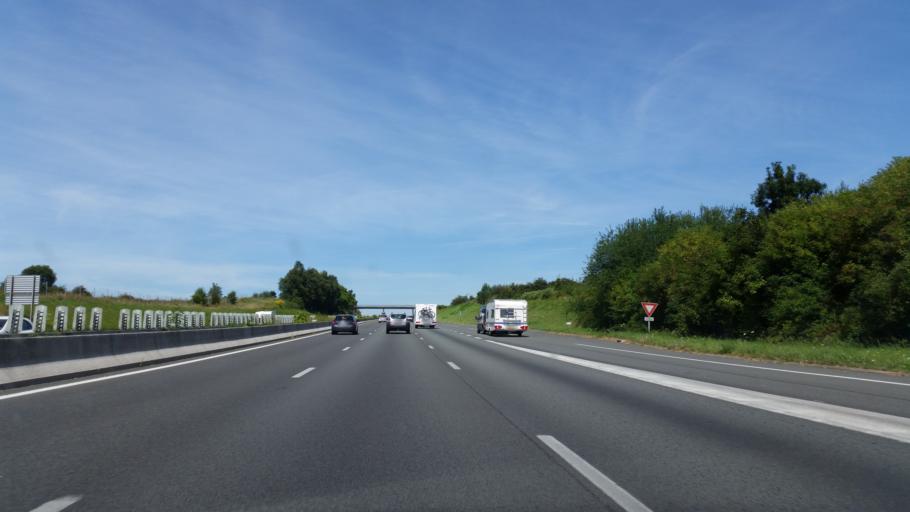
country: FR
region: Nord-Pas-de-Calais
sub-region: Departement du Pas-de-Calais
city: Croisilles
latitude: 50.1949
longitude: 2.8704
